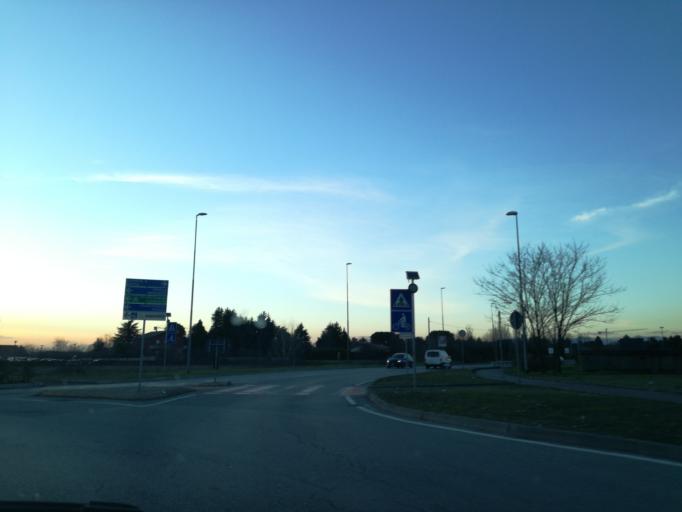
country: IT
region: Lombardy
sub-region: Provincia di Monza e Brianza
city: Vimercate
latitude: 45.6085
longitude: 9.3610
